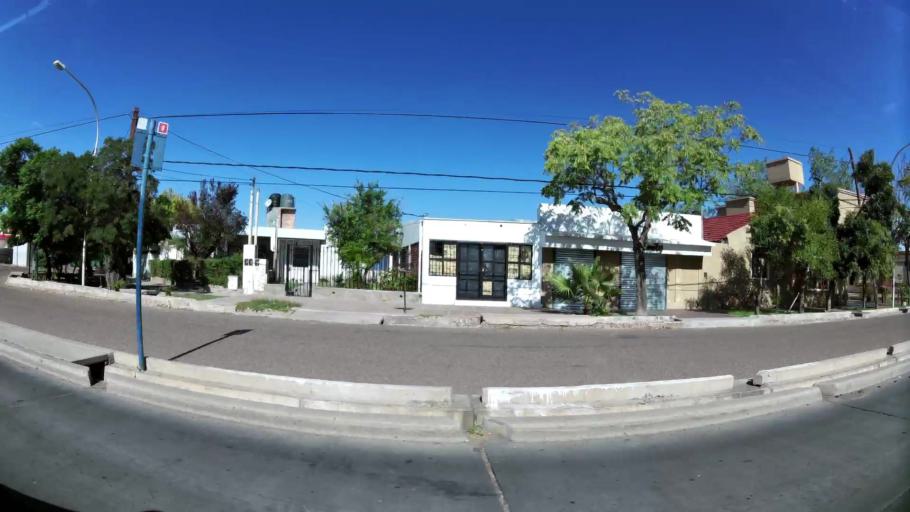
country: AR
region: Mendoza
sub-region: Departamento de Godoy Cruz
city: Godoy Cruz
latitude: -32.9350
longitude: -68.8000
